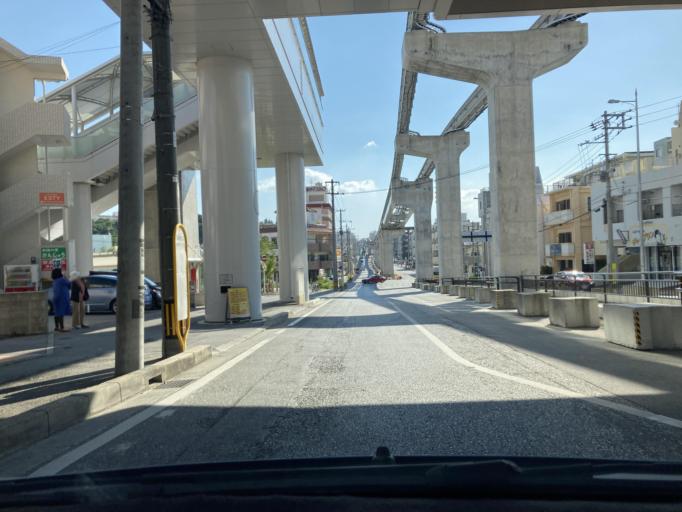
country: JP
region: Okinawa
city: Ginowan
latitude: 26.2269
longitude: 127.7290
